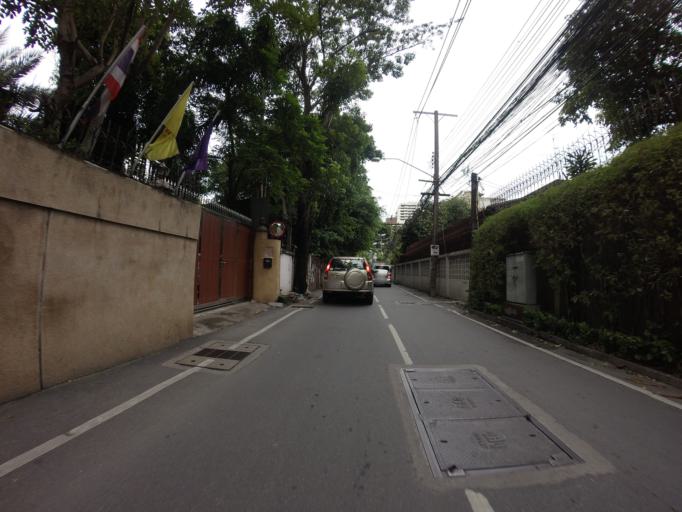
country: TH
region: Bangkok
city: Watthana
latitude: 13.7431
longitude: 100.5697
